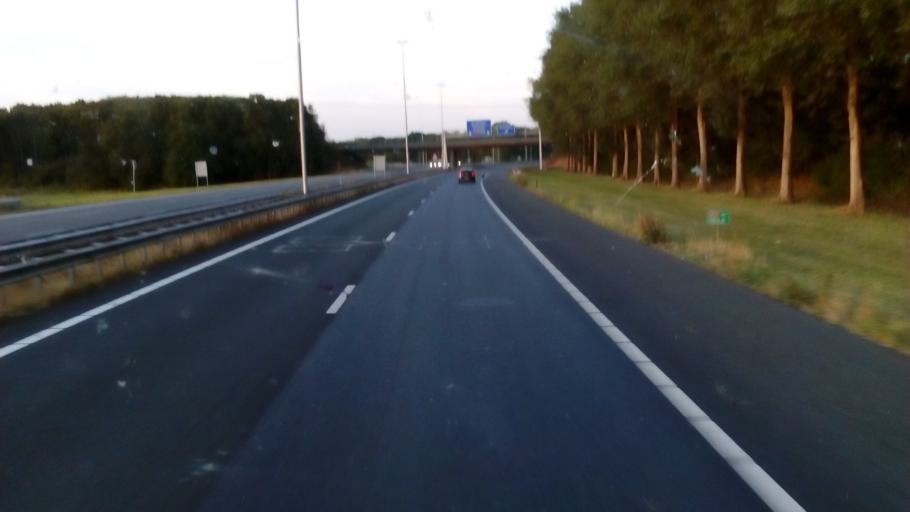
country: NL
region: Gelderland
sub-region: Gemeente Nijmegen
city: Lindenholt
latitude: 51.8366
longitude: 5.7750
